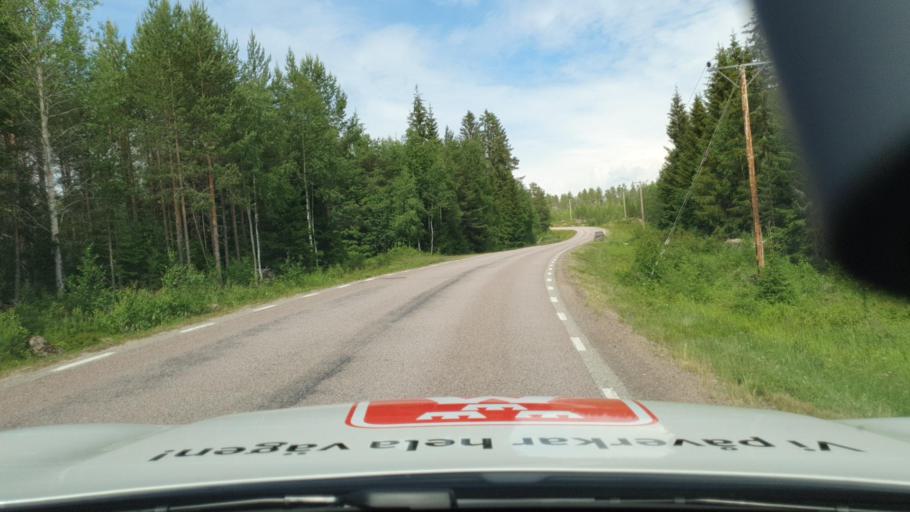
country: NO
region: Hedmark
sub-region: Asnes
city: Flisa
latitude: 60.7167
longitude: 12.6153
